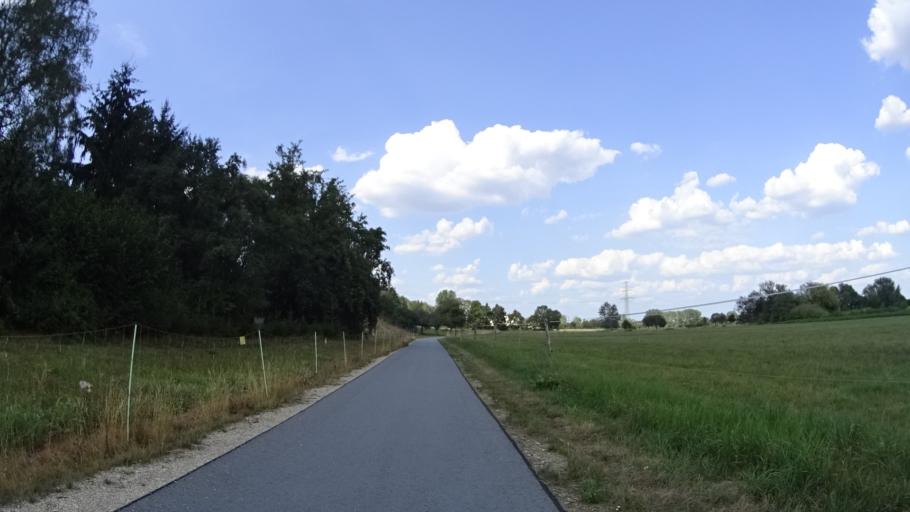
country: DE
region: Saxony
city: Ostritz
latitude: 51.0454
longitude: 14.9516
